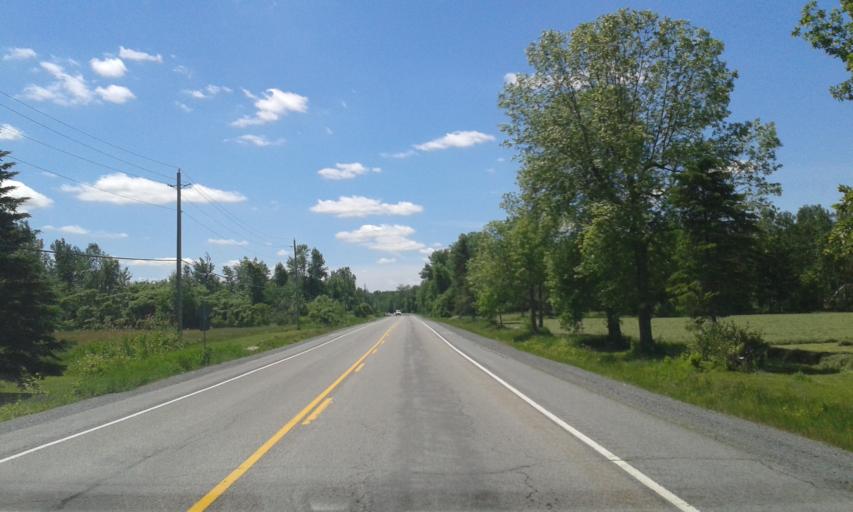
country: CA
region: Ontario
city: Cornwall
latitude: 45.1210
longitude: -74.5095
